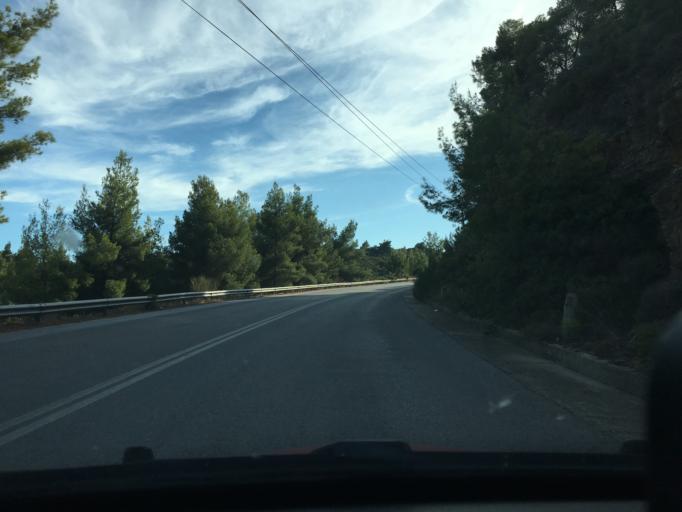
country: GR
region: Central Macedonia
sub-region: Nomos Chalkidikis
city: Agios Nikolaos
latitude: 40.2810
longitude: 23.6852
